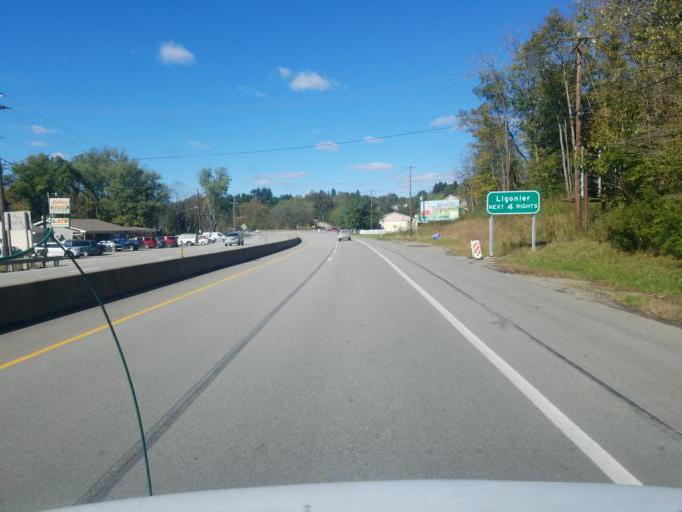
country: US
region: Pennsylvania
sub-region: Westmoreland County
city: Ligonier
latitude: 40.2351
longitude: -79.2284
